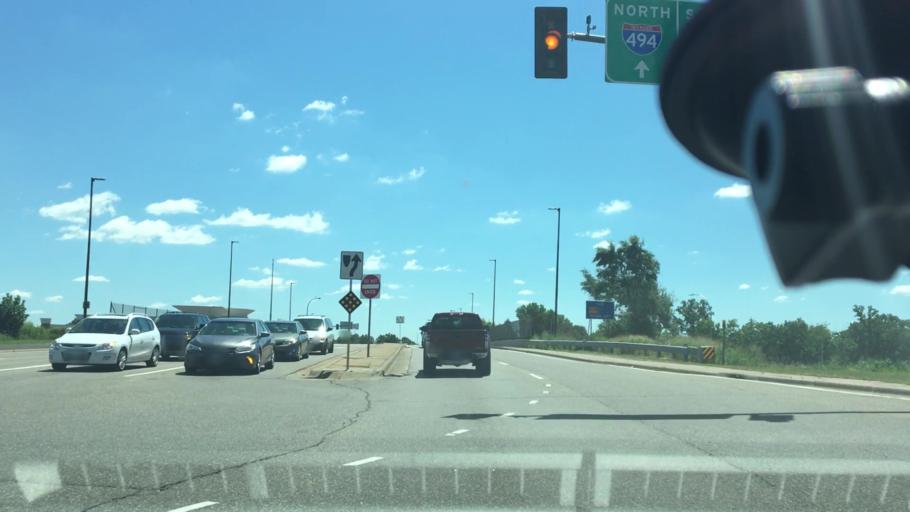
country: US
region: Minnesota
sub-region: Hennepin County
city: Maple Grove
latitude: 45.0674
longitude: -93.4490
